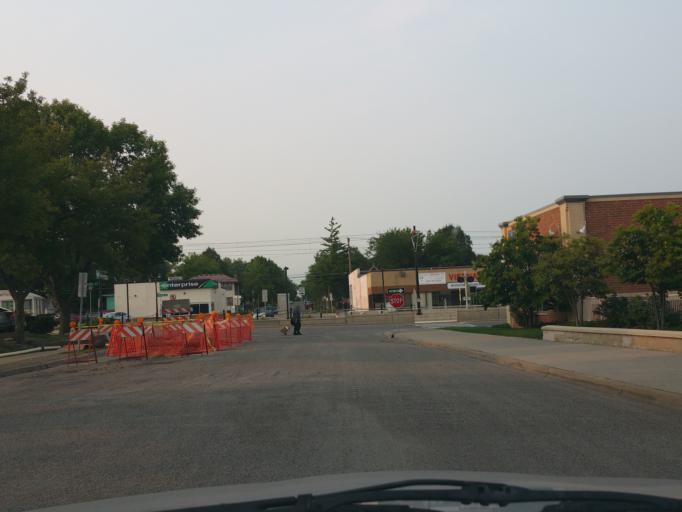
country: US
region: Minnesota
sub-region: Ramsey County
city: Falcon Heights
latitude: 44.9552
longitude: -93.1492
